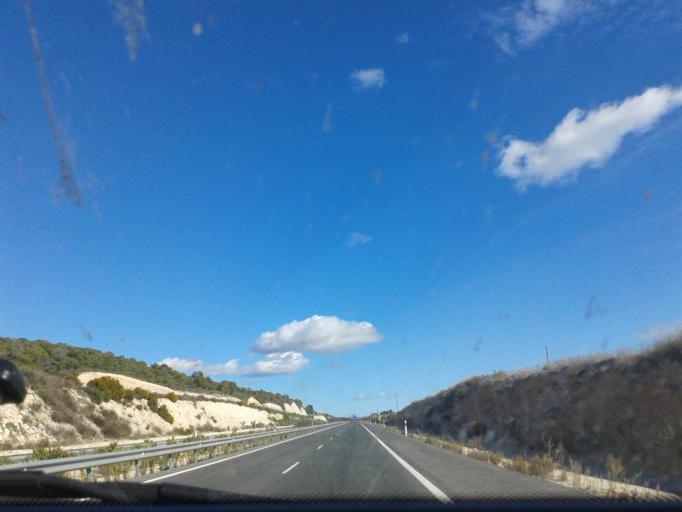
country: ES
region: Valencia
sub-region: Provincia de Alicante
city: Biar
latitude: 38.5892
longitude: -0.7574
